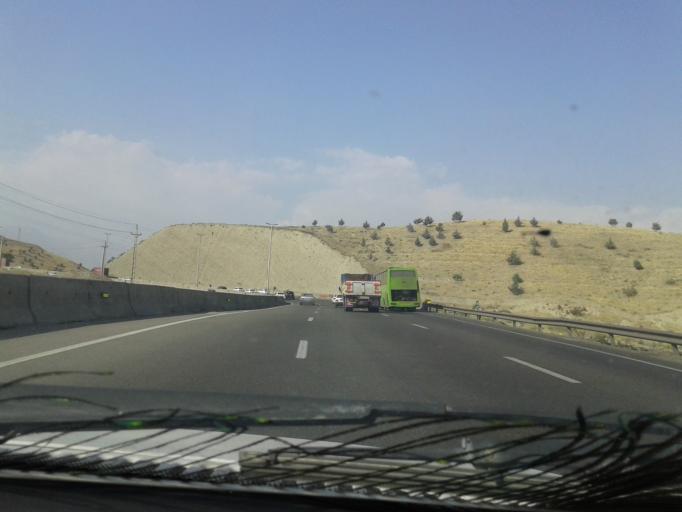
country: IR
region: Tehran
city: Pakdasht
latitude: 35.7364
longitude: 51.6798
